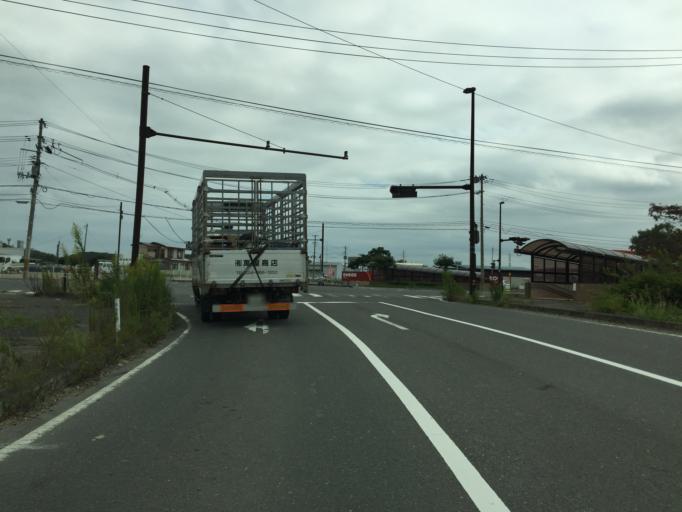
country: JP
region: Fukushima
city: Koriyama
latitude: 37.4589
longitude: 140.3772
